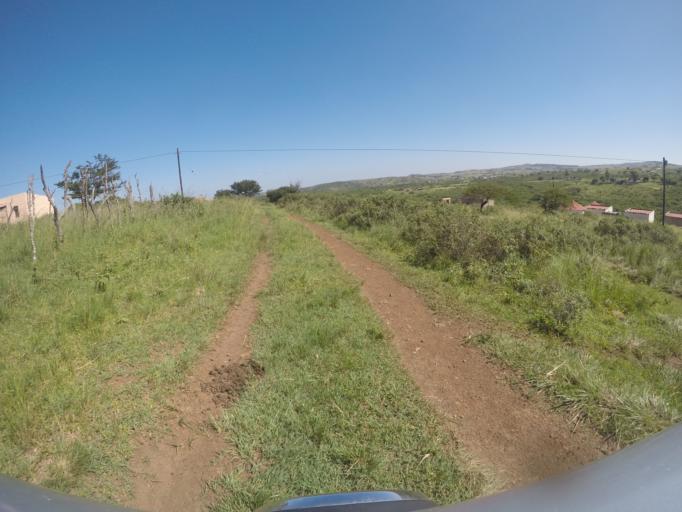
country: ZA
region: KwaZulu-Natal
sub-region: uThungulu District Municipality
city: Empangeni
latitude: -28.5693
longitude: 31.6987
